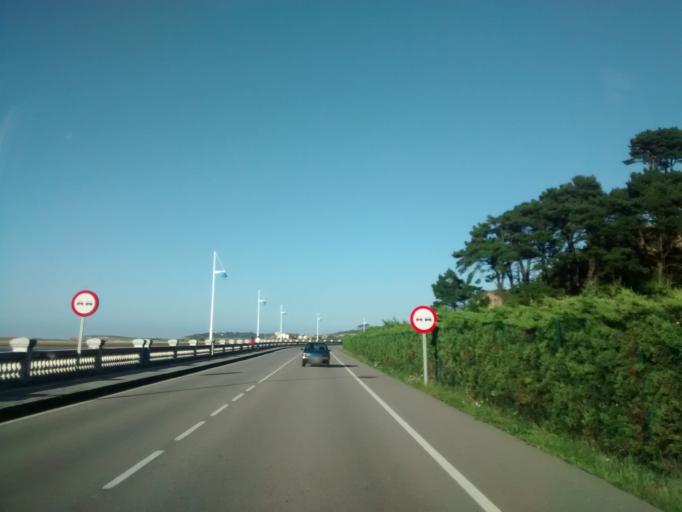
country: ES
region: Cantabria
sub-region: Provincia de Cantabria
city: Santander
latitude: 43.4475
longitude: -3.7619
